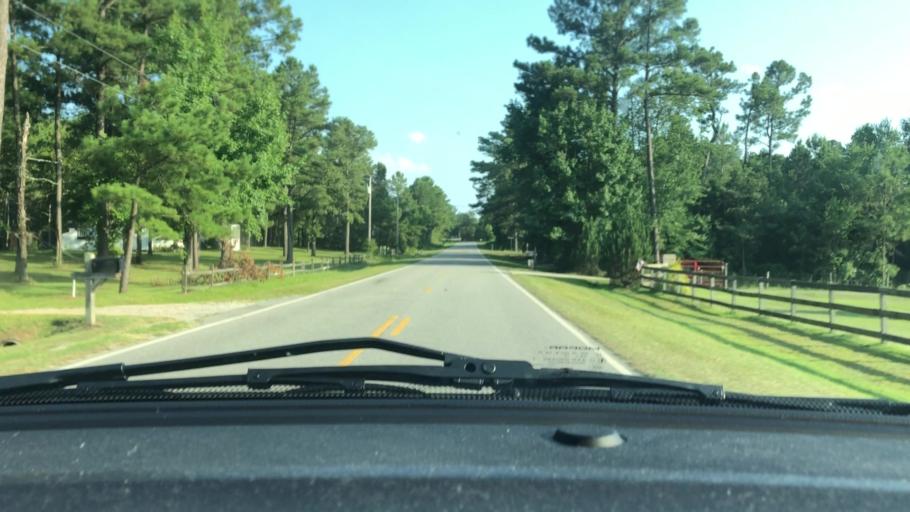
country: US
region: North Carolina
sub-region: Lee County
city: Broadway
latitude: 35.3287
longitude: -79.0719
